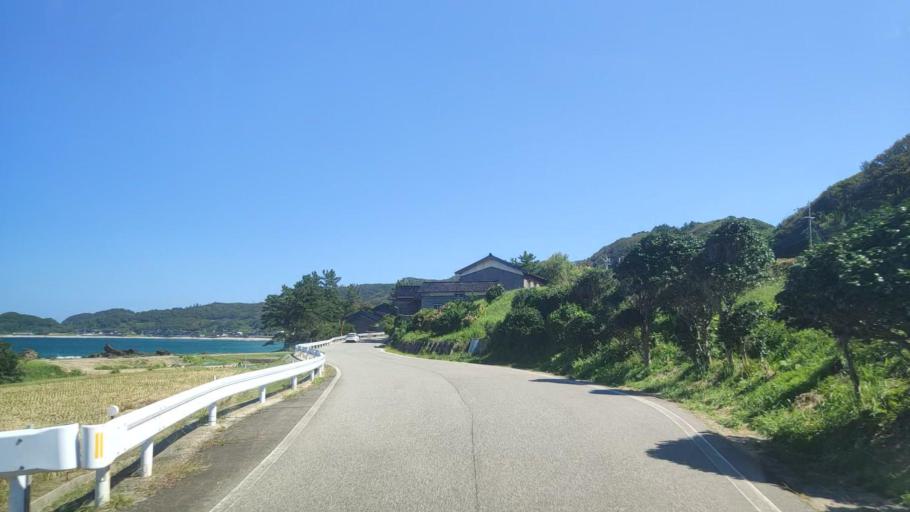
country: JP
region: Ishikawa
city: Nanao
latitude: 37.5057
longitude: 137.2047
